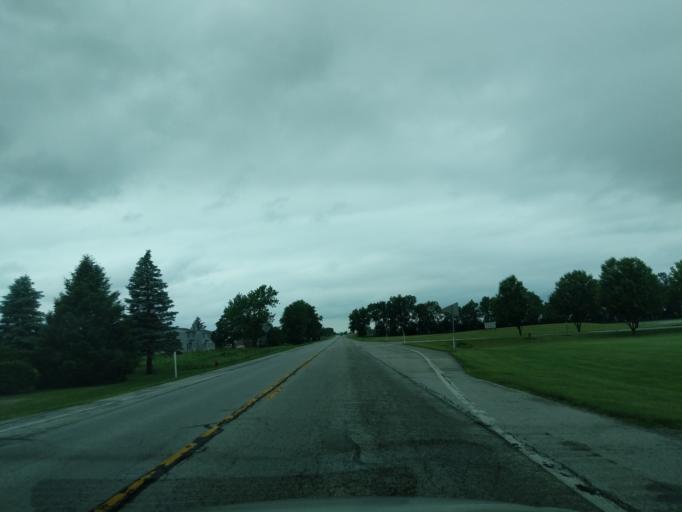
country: US
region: Indiana
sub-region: Hamilton County
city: Arcadia
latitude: 40.1806
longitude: -86.0155
